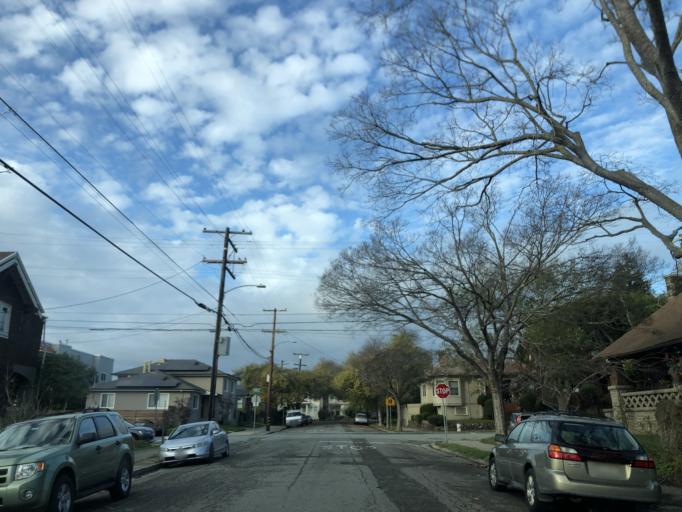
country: US
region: California
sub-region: Alameda County
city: Berkeley
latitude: 37.8478
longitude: -122.2598
